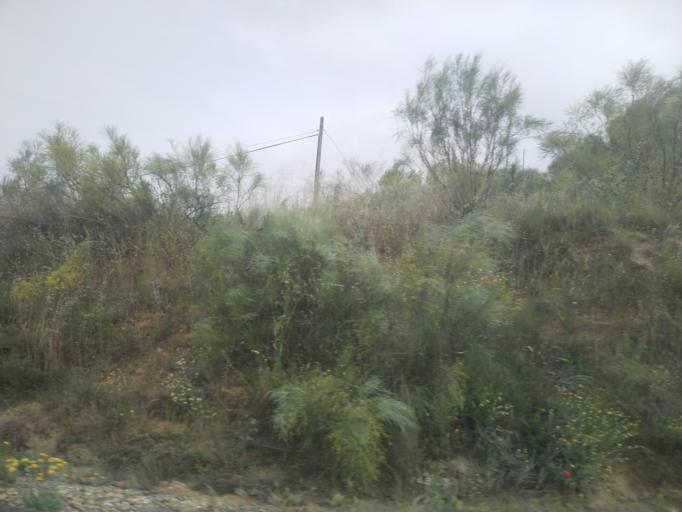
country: ES
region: Castille-La Mancha
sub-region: Province of Toledo
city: Guadamur
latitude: 39.8117
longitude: -4.1143
